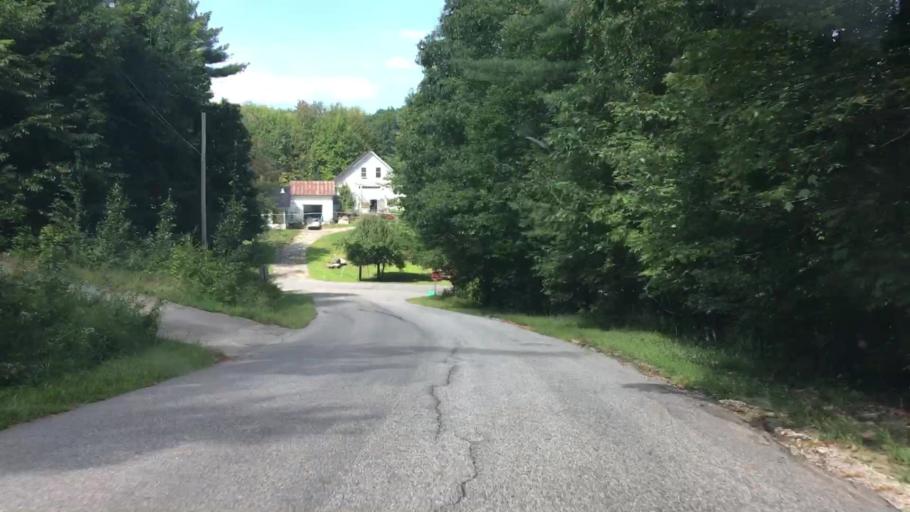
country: US
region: Maine
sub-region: Kennebec County
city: Monmouth
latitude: 44.2746
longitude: -70.0334
